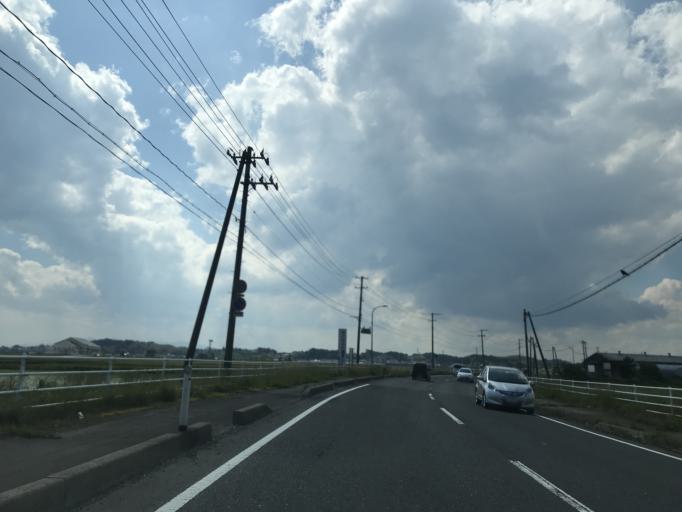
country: JP
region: Miyagi
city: Wakuya
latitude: 38.4750
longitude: 141.1152
